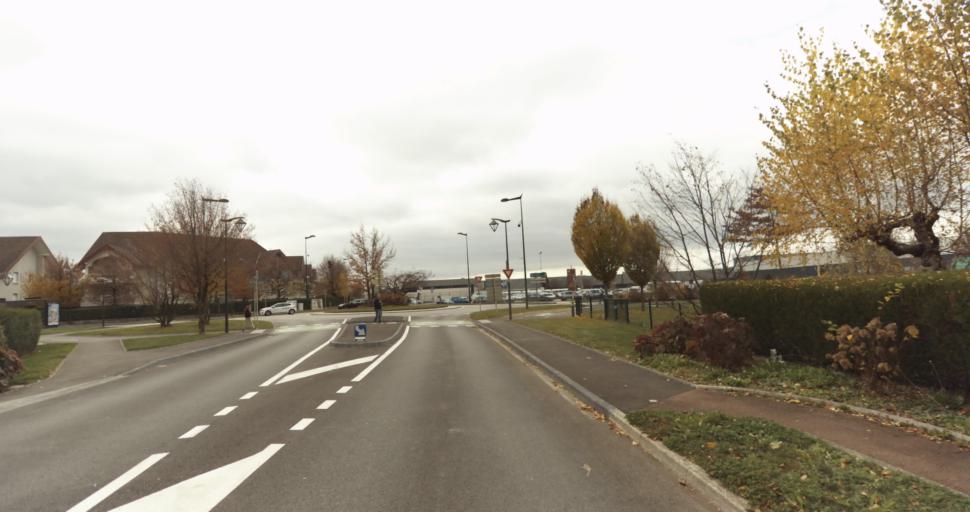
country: FR
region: Rhone-Alpes
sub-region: Departement de la Haute-Savoie
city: Pringy
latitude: 45.9410
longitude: 6.1360
